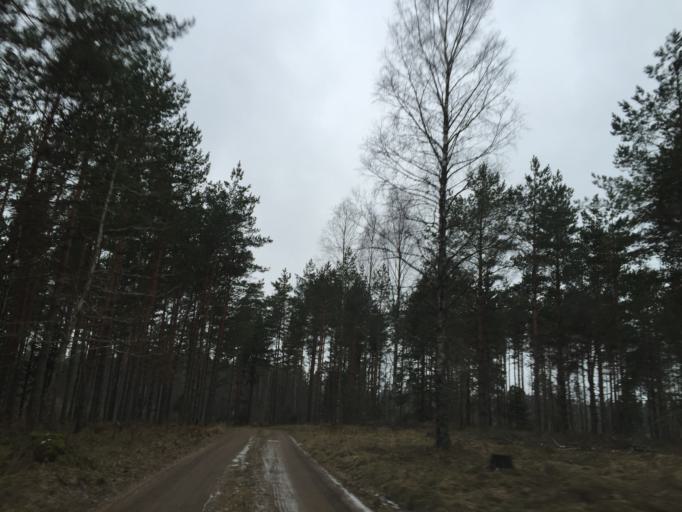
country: EE
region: Saare
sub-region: Kuressaare linn
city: Kuressaare
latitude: 58.3863
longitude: 22.2532
